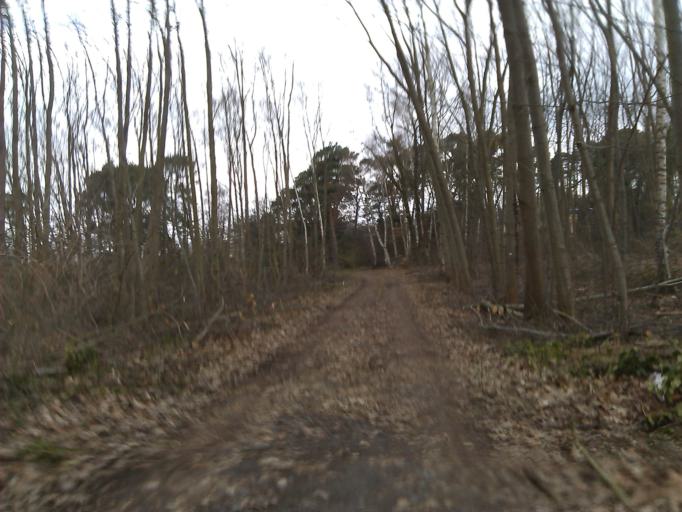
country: DE
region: Hesse
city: Griesheim
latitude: 49.8280
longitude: 8.5656
